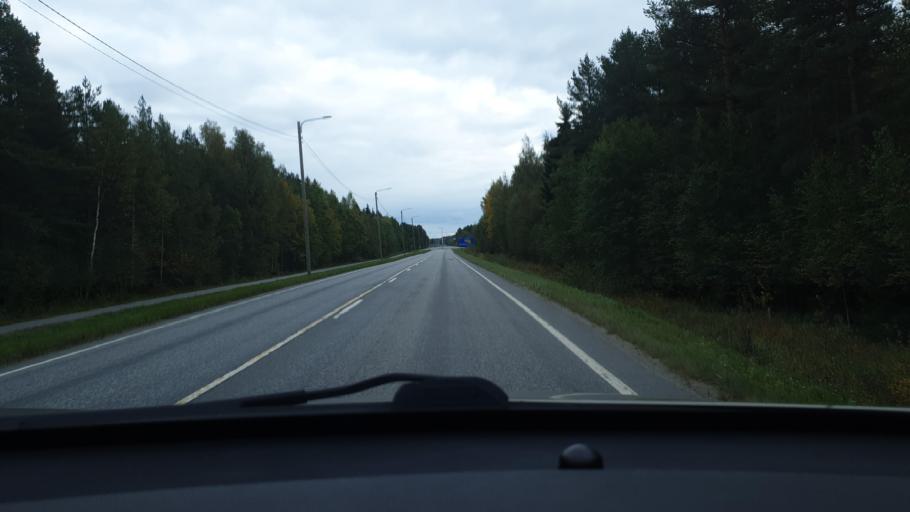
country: FI
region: Ostrobothnia
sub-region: Vaasa
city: Ristinummi
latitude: 63.0578
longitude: 21.7143
